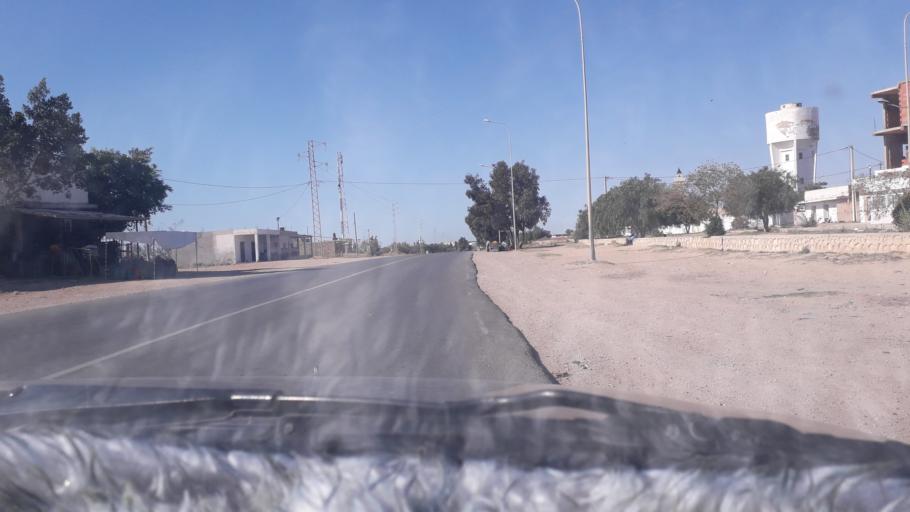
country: TN
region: Safaqis
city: Al Qarmadah
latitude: 34.8857
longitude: 10.7621
